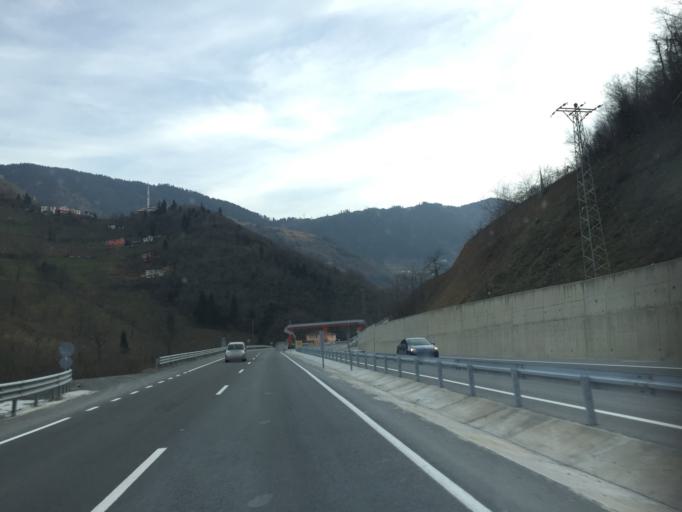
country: TR
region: Trabzon
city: Macka
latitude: 40.7624
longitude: 39.5630
